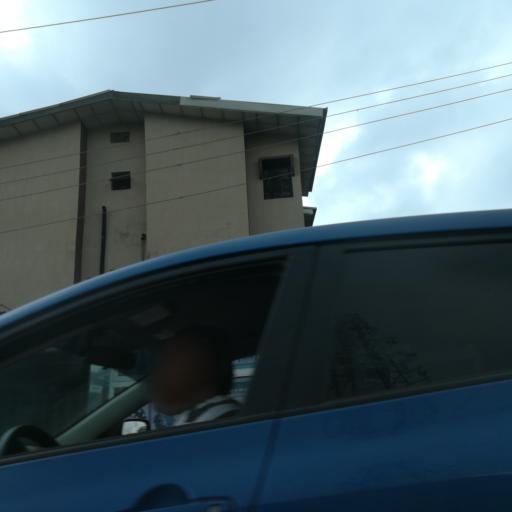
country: NG
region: Lagos
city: Agege
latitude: 6.5976
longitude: 3.2998
